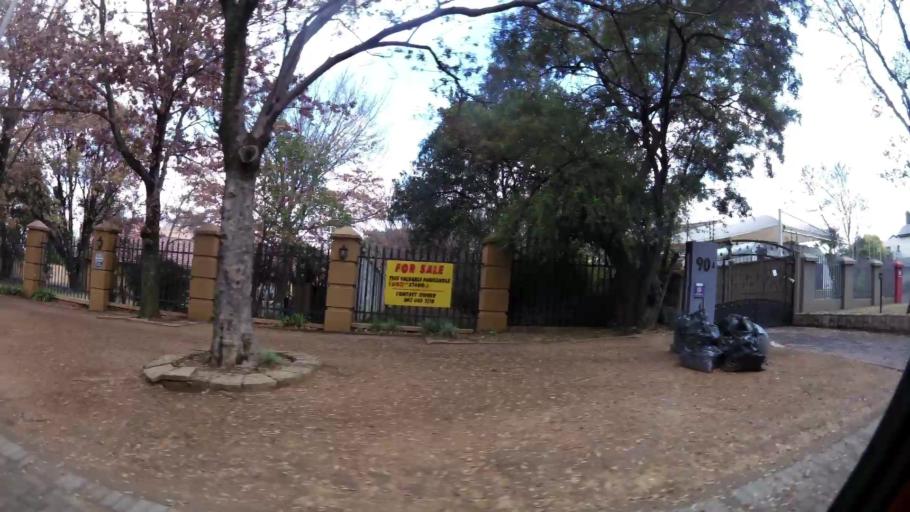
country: ZA
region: Gauteng
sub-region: Sedibeng District Municipality
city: Vanderbijlpark
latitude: -26.7406
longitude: 27.8275
